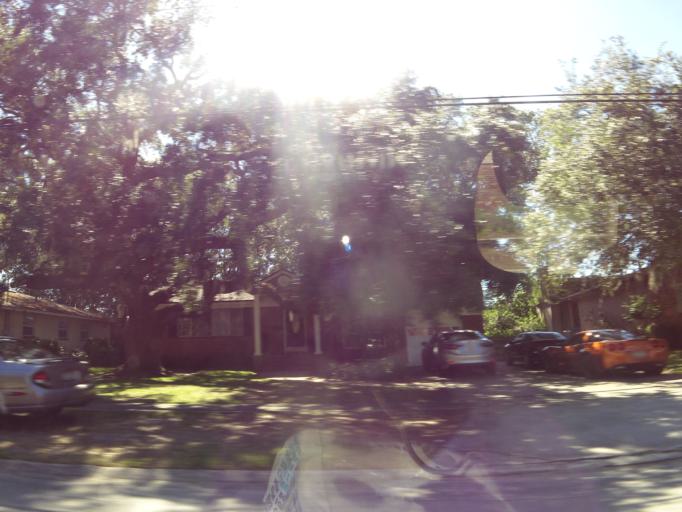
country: US
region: Florida
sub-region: Duval County
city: Jacksonville
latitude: 30.3401
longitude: -81.5685
